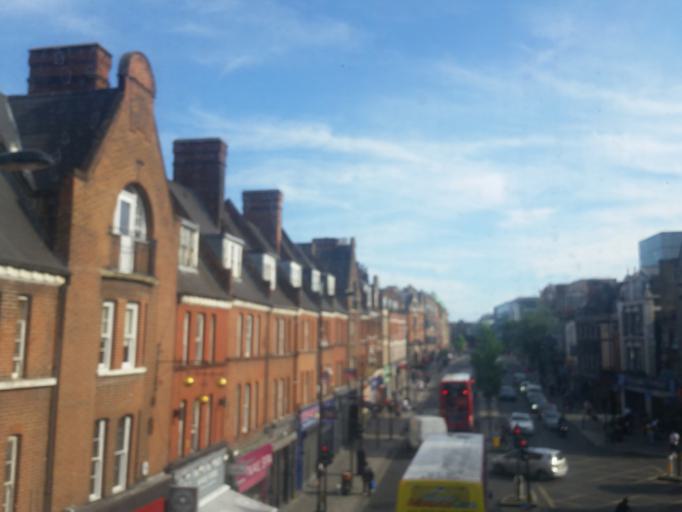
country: GB
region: England
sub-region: Greater London
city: Hackney
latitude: 51.5471
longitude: -0.0550
